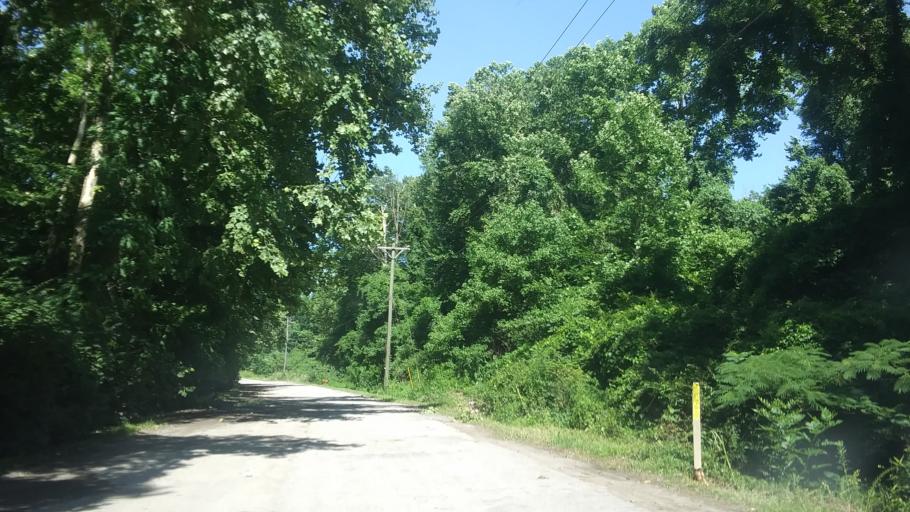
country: US
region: Tennessee
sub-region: Davidson County
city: Oak Hill
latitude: 36.0916
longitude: -86.6798
